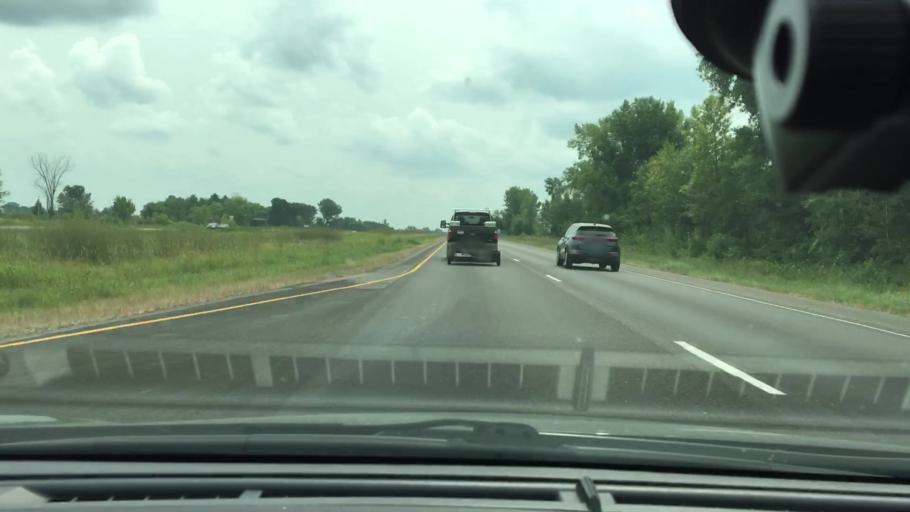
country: US
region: Minnesota
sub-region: Mille Lacs County
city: Princeton
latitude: 45.6127
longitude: -93.6097
